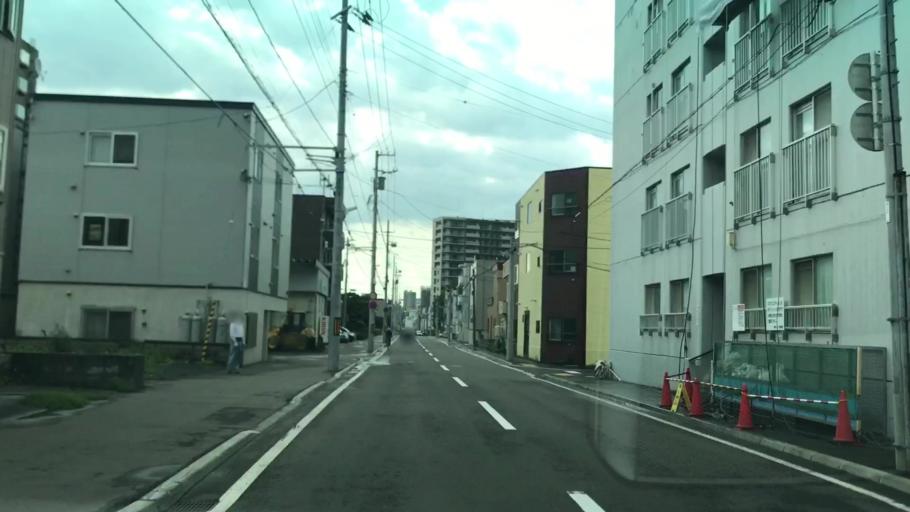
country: JP
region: Hokkaido
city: Sapporo
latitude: 43.0753
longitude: 141.3086
